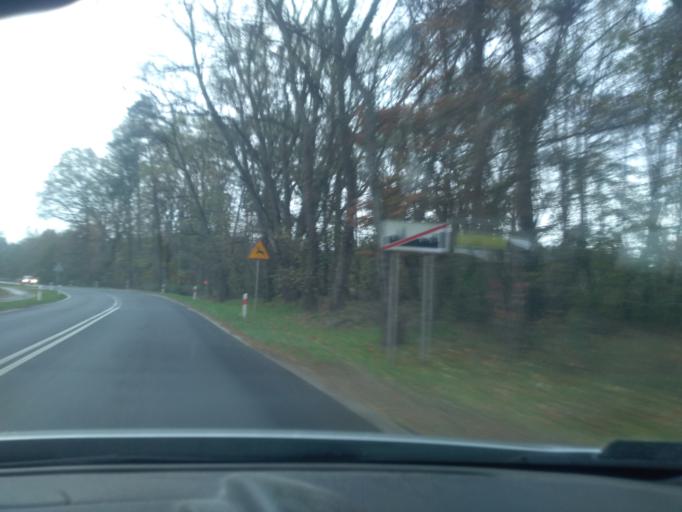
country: PL
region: Greater Poland Voivodeship
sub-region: Powiat poznanski
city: Murowana Goslina
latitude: 52.5349
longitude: 16.9433
